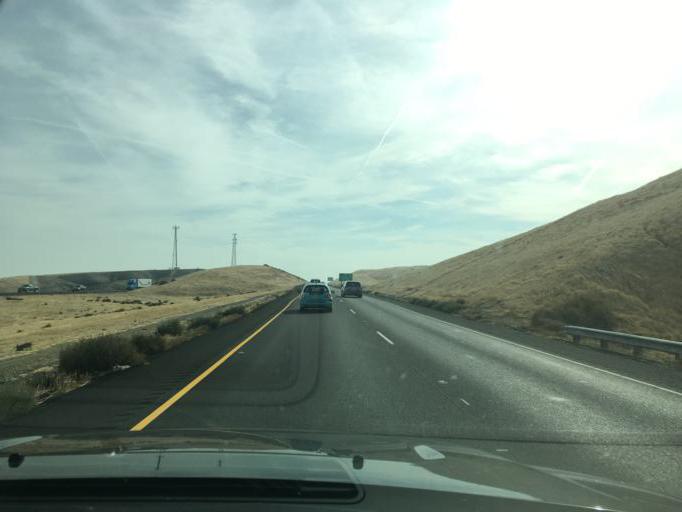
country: US
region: California
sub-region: Kings County
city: Kettleman City
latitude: 35.9916
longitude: -119.9708
